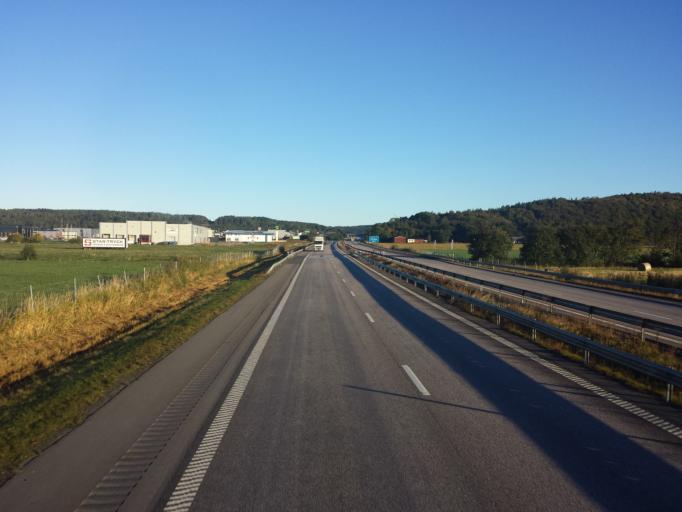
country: SE
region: Halland
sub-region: Varbergs Kommun
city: Varberg
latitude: 57.1590
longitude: 12.2872
